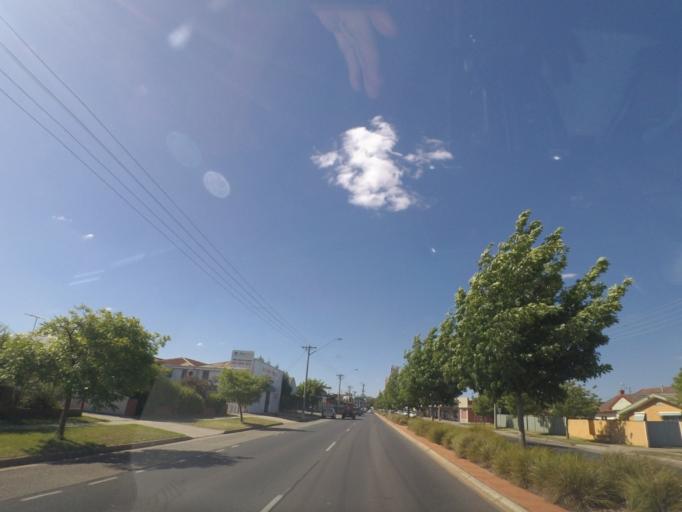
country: AU
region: New South Wales
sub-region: Albury Municipality
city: North Albury
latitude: -36.0550
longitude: 146.9331
